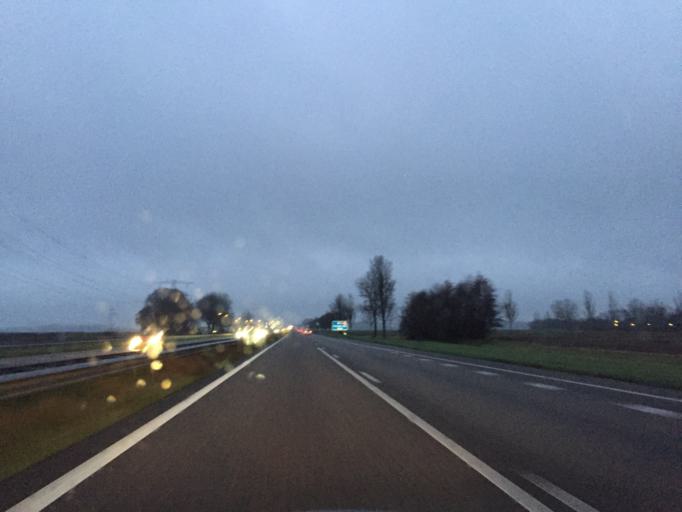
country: NL
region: North Brabant
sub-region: Roosendaal
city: Roosendaal
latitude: 51.5935
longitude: 4.4949
